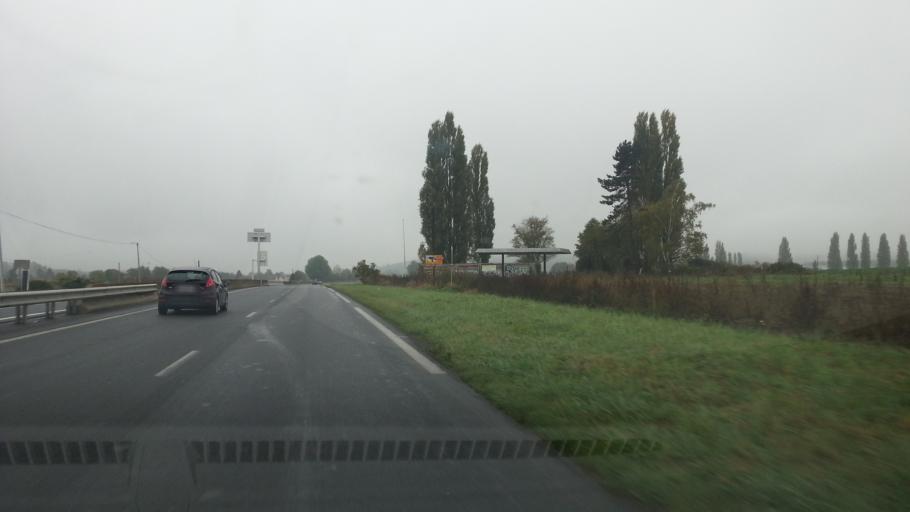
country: FR
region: Picardie
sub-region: Departement de l'Oise
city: Breuil-le-Vert
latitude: 49.3450
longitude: 2.4316
